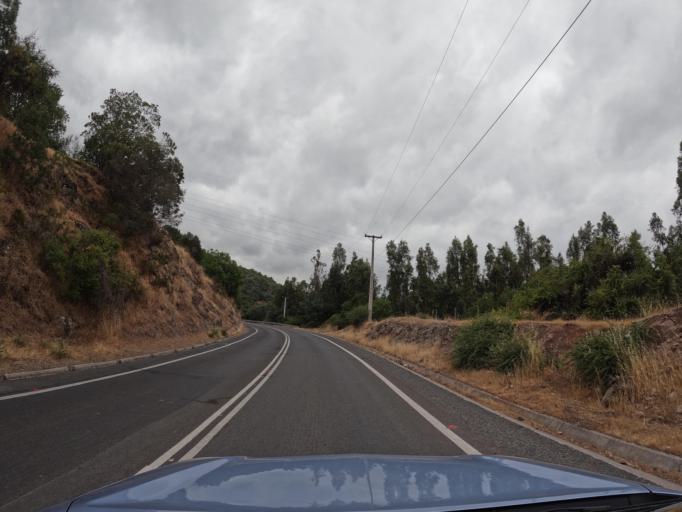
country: CL
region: O'Higgins
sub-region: Provincia de Colchagua
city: Chimbarongo
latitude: -34.7287
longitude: -71.0946
